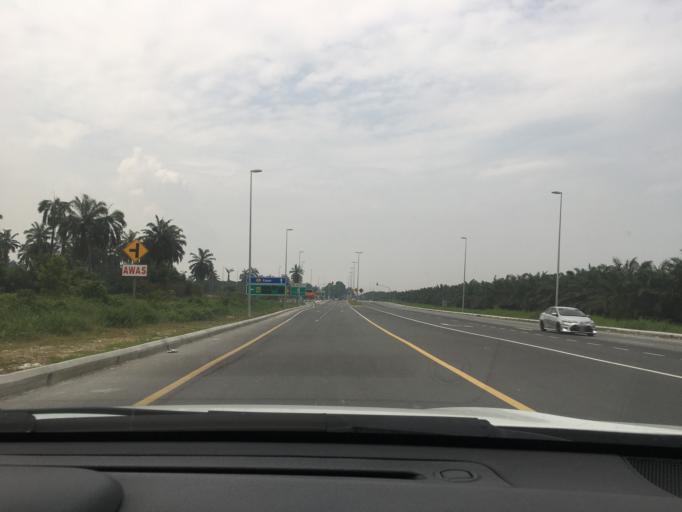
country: MY
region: Selangor
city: Klang
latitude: 3.1361
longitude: 101.3991
